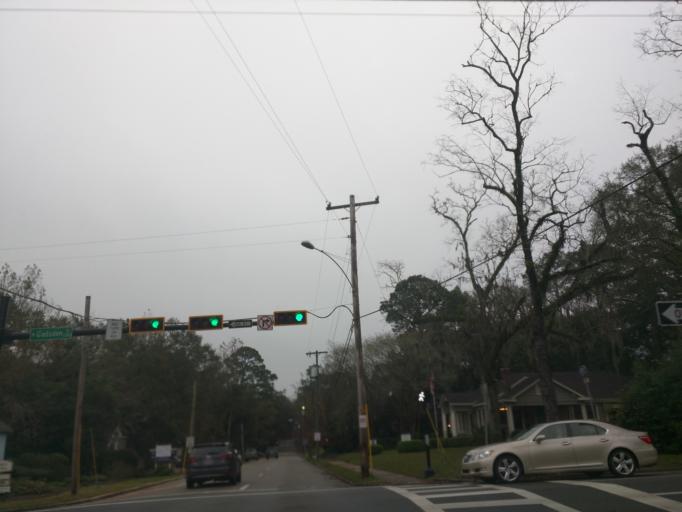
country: US
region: Florida
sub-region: Leon County
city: Tallahassee
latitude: 30.4563
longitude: -84.2766
